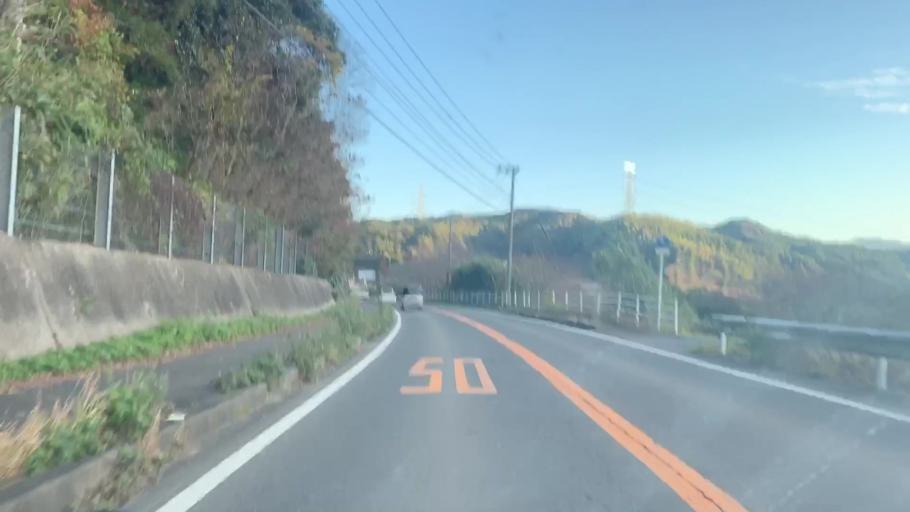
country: JP
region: Saga Prefecture
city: Karatsu
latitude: 33.3648
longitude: 130.0069
